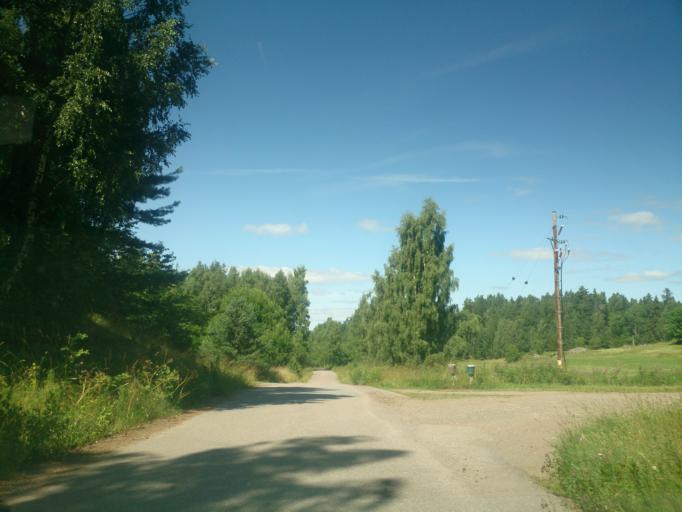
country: SE
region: OEstergoetland
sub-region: Atvidabergs Kommun
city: Atvidaberg
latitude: 58.2356
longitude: 15.9658
